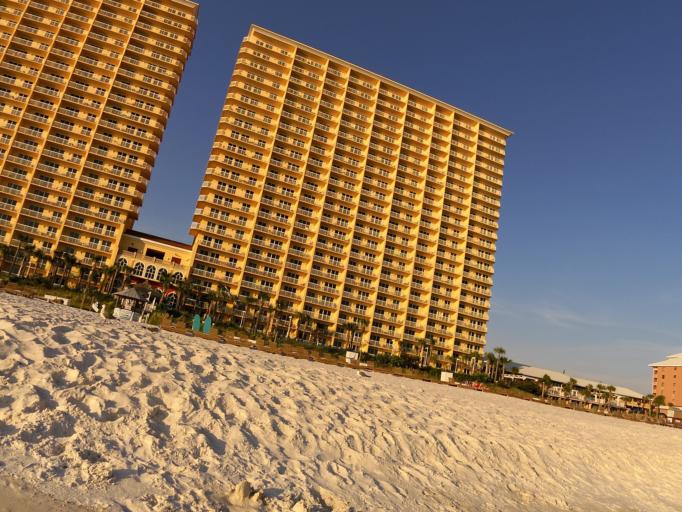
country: US
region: Florida
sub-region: Bay County
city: Laguna Beach
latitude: 30.2132
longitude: -85.8748
